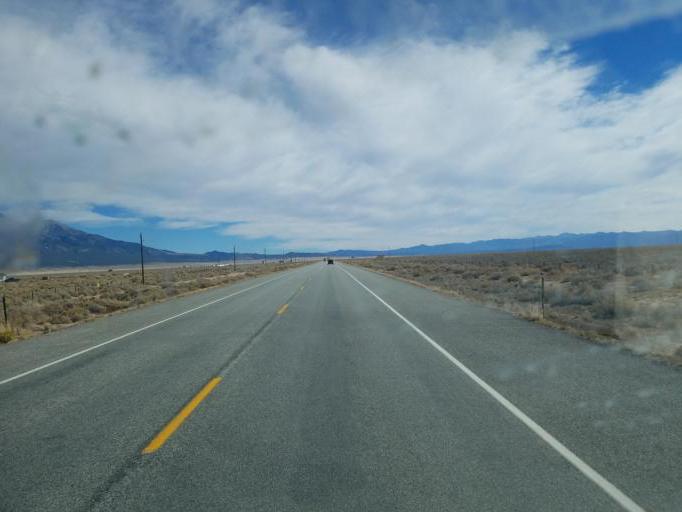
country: US
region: Colorado
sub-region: Alamosa County
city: Alamosa East
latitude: 37.4746
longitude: -105.6795
